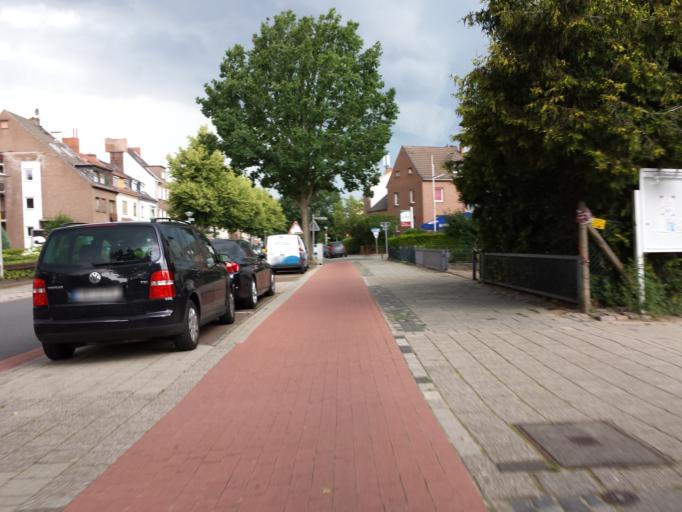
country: DE
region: Bremen
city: Bremen
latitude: 53.0806
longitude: 8.7678
